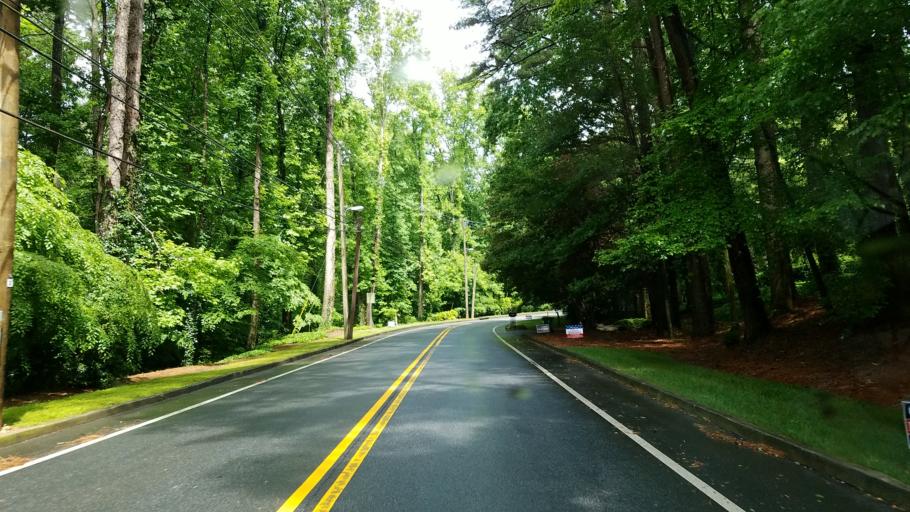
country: US
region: Georgia
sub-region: Fulton County
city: Sandy Springs
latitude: 33.9147
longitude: -84.4340
